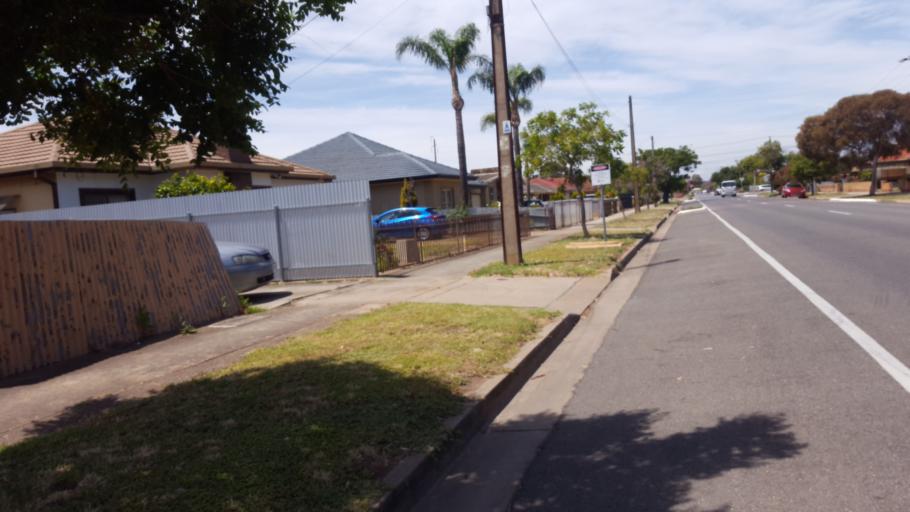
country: AU
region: South Australia
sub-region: Port Adelaide Enfield
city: Alberton
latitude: -34.8470
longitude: 138.5321
